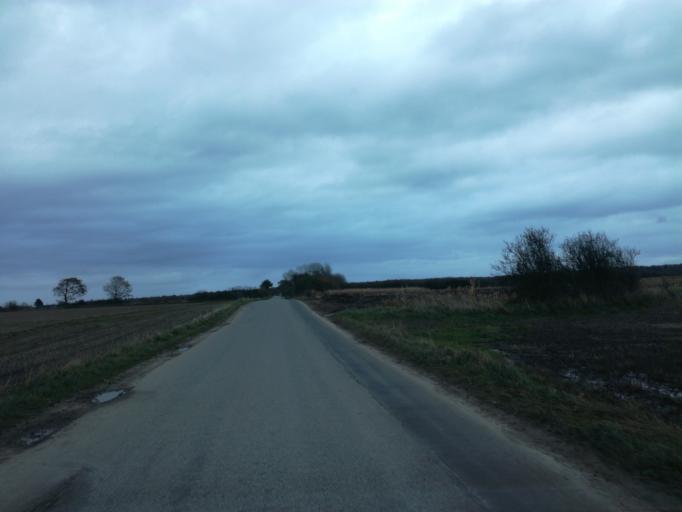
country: DK
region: South Denmark
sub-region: Fredericia Kommune
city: Fredericia
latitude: 55.6133
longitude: 9.7825
